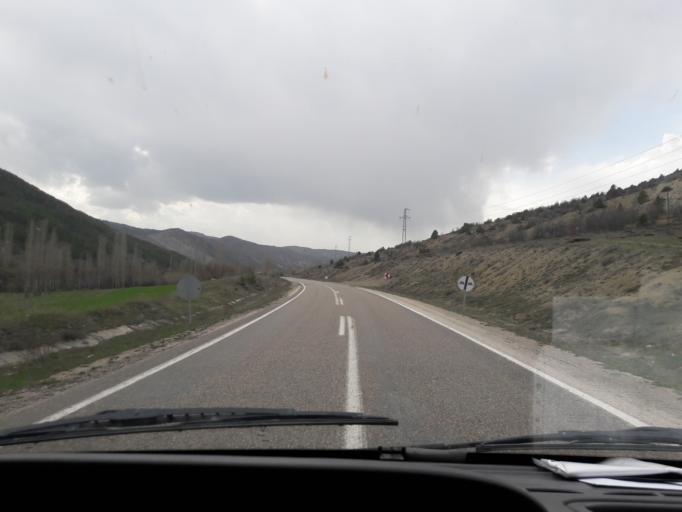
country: TR
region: Giresun
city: Alucra
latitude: 40.2743
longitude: 38.8556
